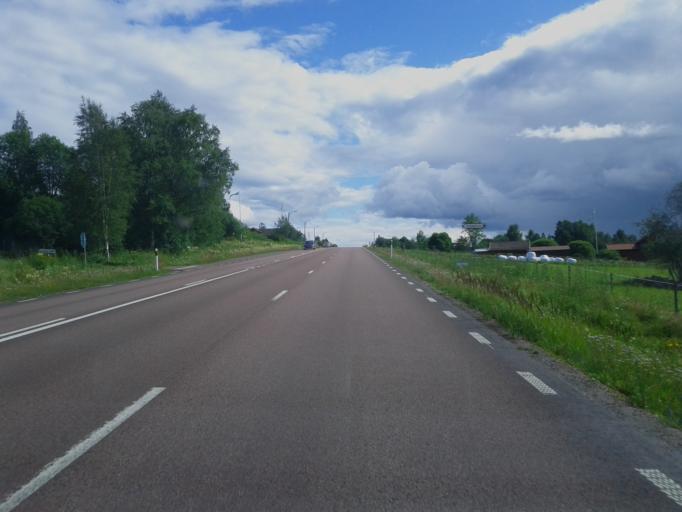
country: SE
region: Dalarna
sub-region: Rattviks Kommun
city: Raettvik
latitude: 60.8576
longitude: 15.1078
